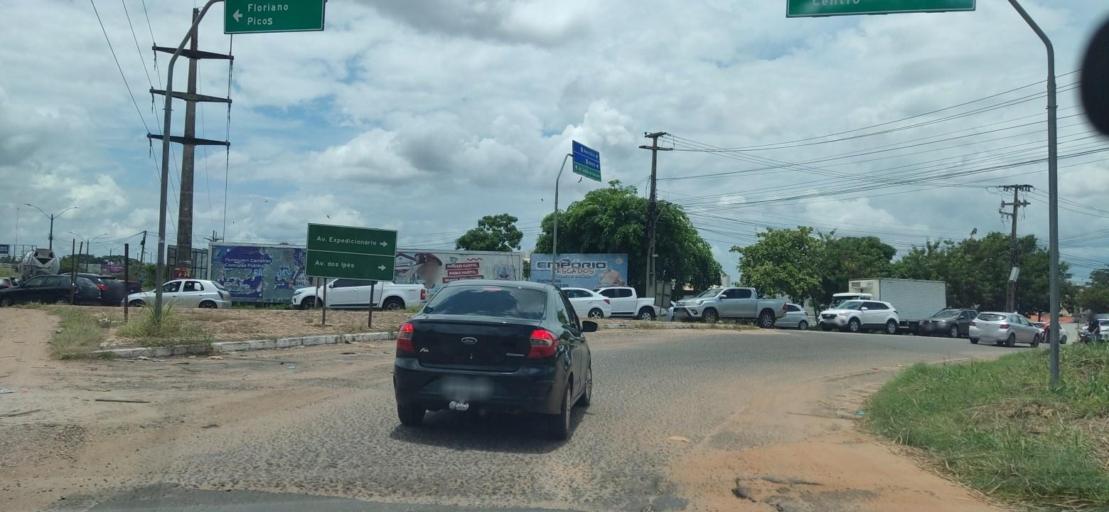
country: BR
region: Piaui
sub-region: Teresina
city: Teresina
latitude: -5.0900
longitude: -42.7608
